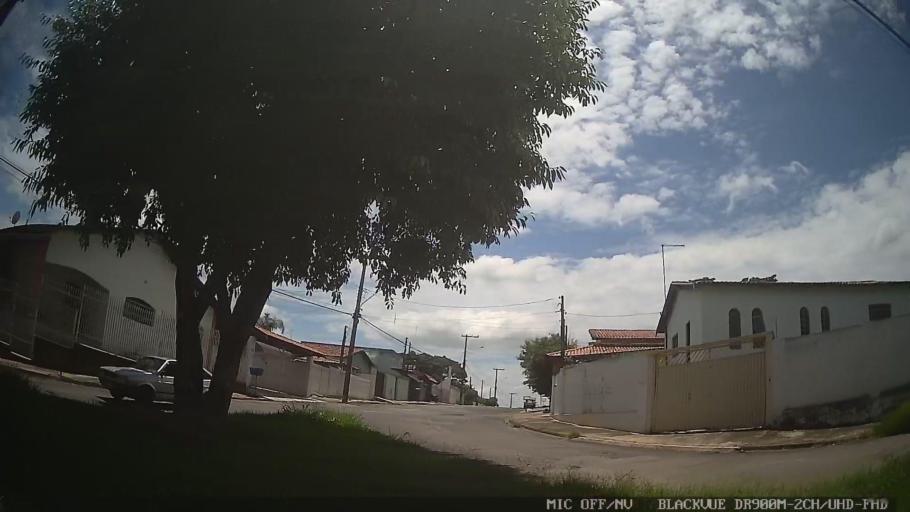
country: BR
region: Sao Paulo
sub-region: Laranjal Paulista
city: Laranjal Paulista
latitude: -23.0323
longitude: -47.8375
